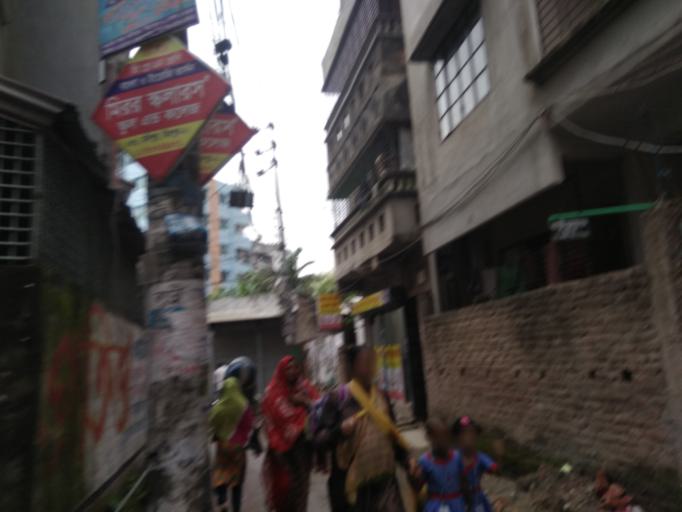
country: BD
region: Dhaka
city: Azimpur
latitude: 23.7981
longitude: 90.3699
